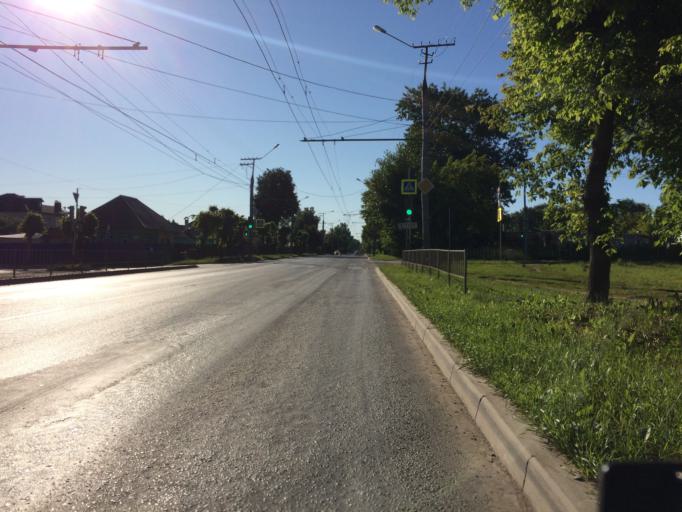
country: RU
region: Mariy-El
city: Yoshkar-Ola
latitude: 56.6522
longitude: 47.8843
